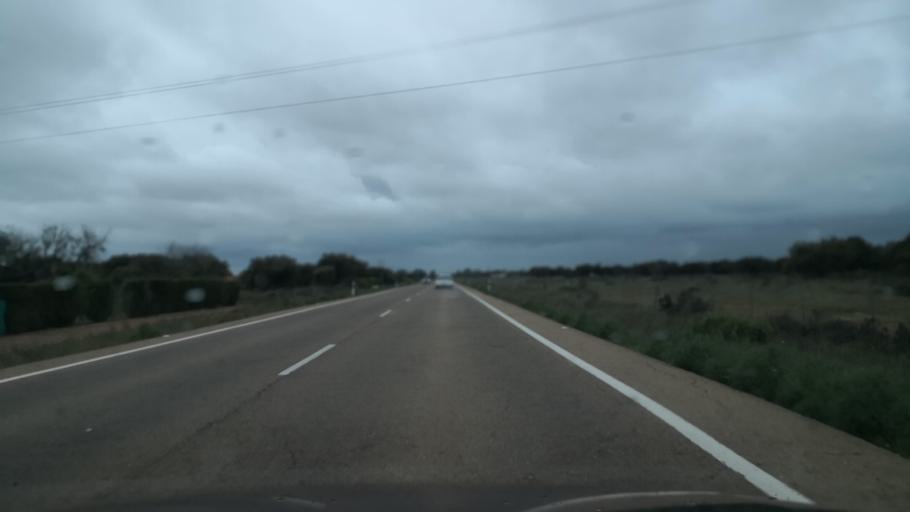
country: ES
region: Extremadura
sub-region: Provincia de Badajoz
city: Villar del Rey
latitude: 38.9984
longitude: -6.8677
